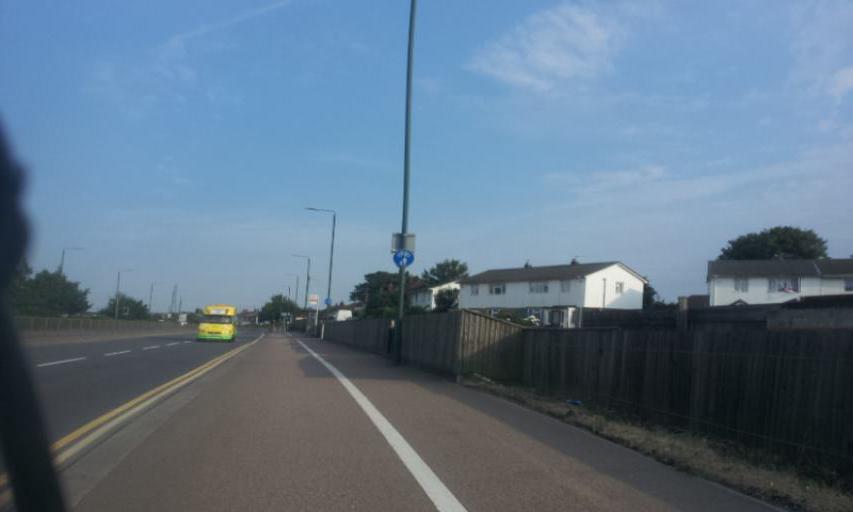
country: GB
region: England
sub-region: Greater London
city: Erith
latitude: 51.4591
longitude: 0.1923
